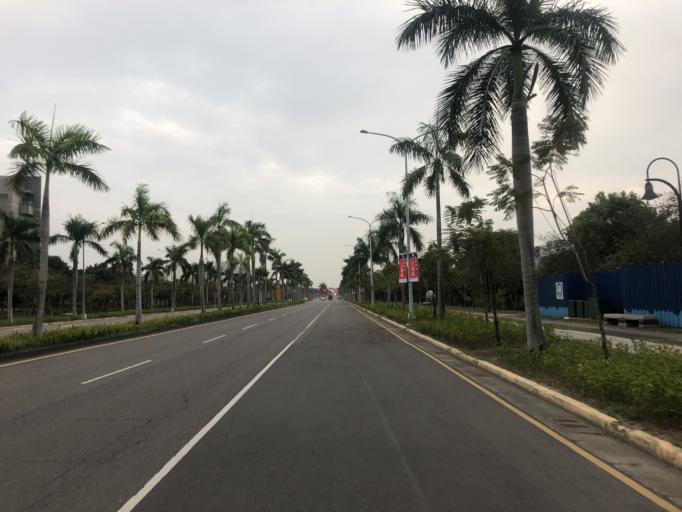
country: TW
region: Taiwan
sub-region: Tainan
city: Tainan
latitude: 23.1016
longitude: 120.2802
